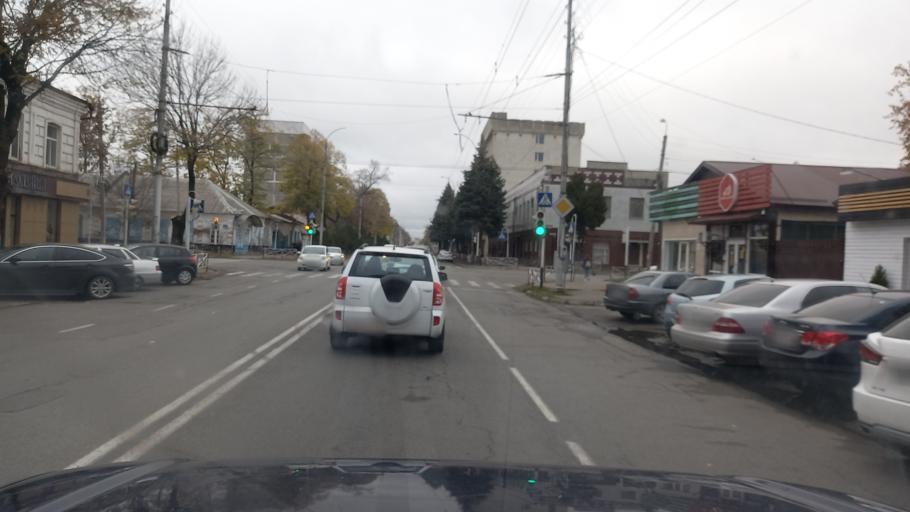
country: RU
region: Adygeya
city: Maykop
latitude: 44.6118
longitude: 40.1081
